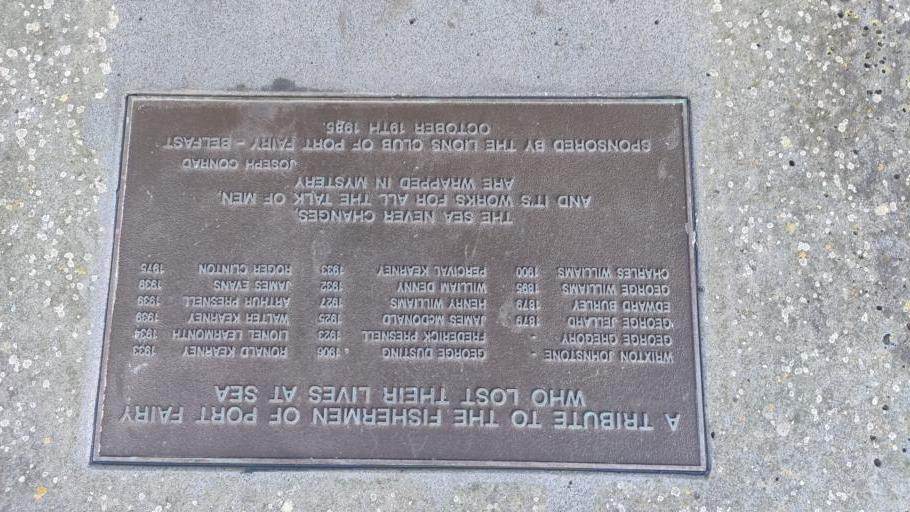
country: AU
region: Victoria
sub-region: Moyne
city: Port Fairy
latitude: -38.3901
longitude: 142.2435
